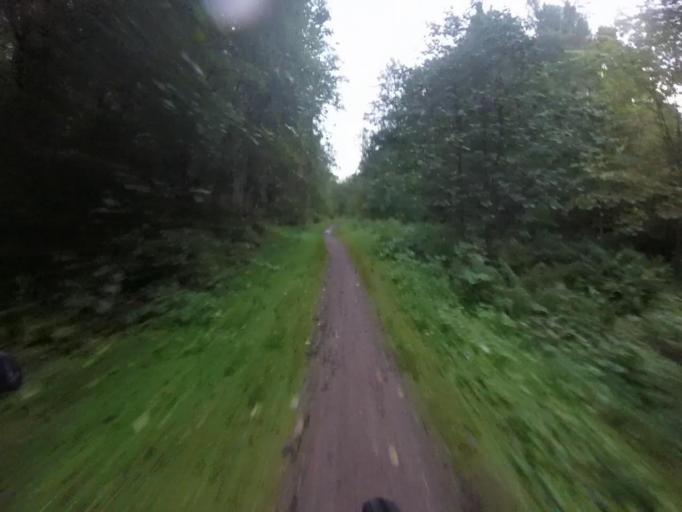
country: SE
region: Vaestra Goetaland
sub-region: Trollhattan
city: Trollhattan
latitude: 58.2787
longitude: 12.2591
